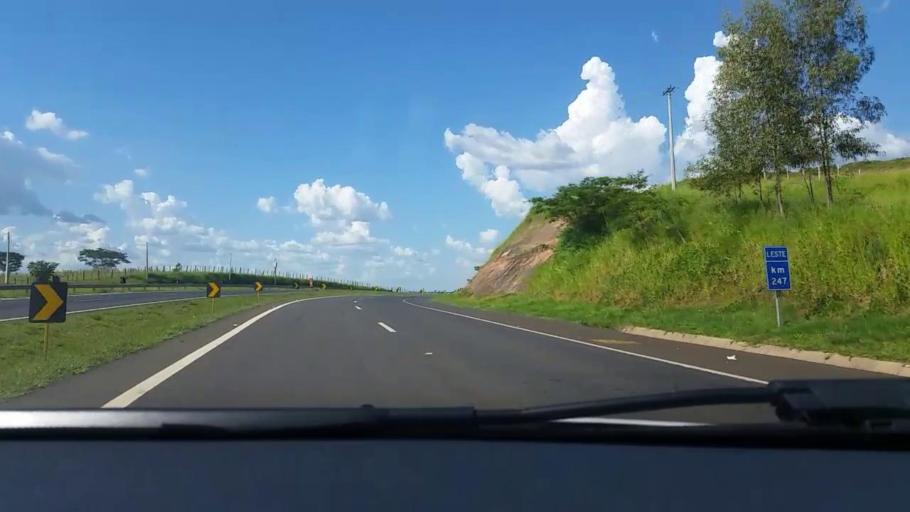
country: BR
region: Sao Paulo
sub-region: Bauru
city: Bauru
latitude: -22.4292
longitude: -49.1318
